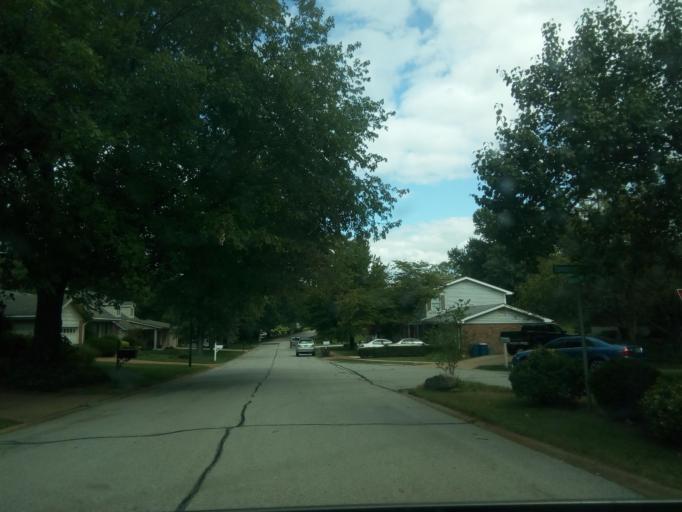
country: US
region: Missouri
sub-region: Saint Louis County
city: Ballwin
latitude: 38.5993
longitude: -90.5464
